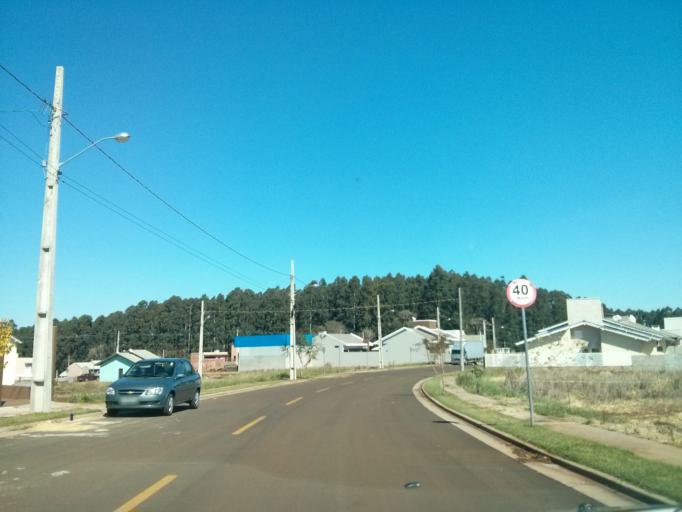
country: BR
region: Santa Catarina
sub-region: Chapeco
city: Chapeco
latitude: -27.0902
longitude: -52.7125
